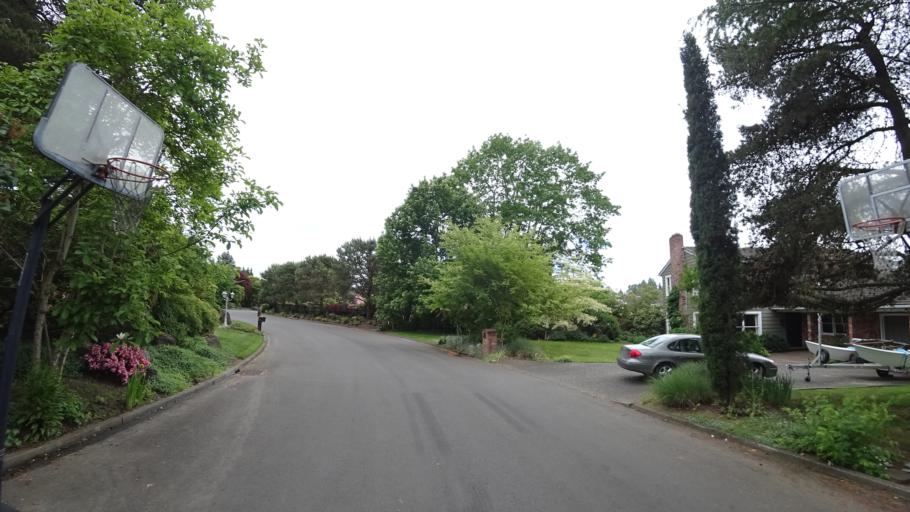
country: US
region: Oregon
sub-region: Washington County
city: Raleigh Hills
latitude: 45.4796
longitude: -122.7580
